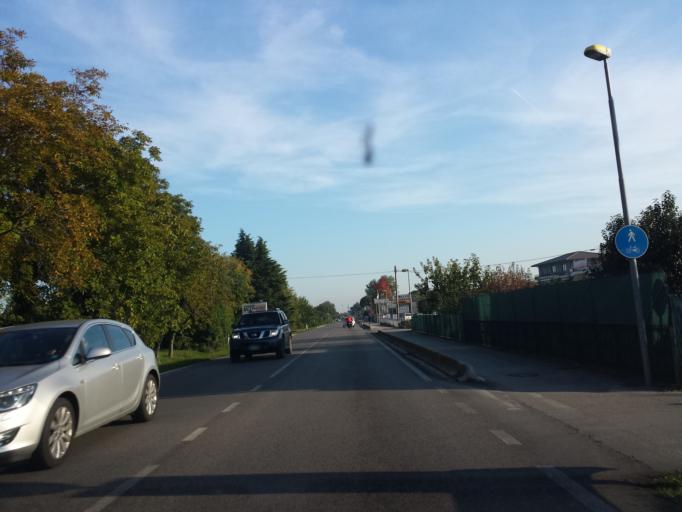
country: IT
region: Veneto
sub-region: Provincia di Vicenza
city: San Vito di Leguzzano
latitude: 45.6935
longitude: 11.3888
